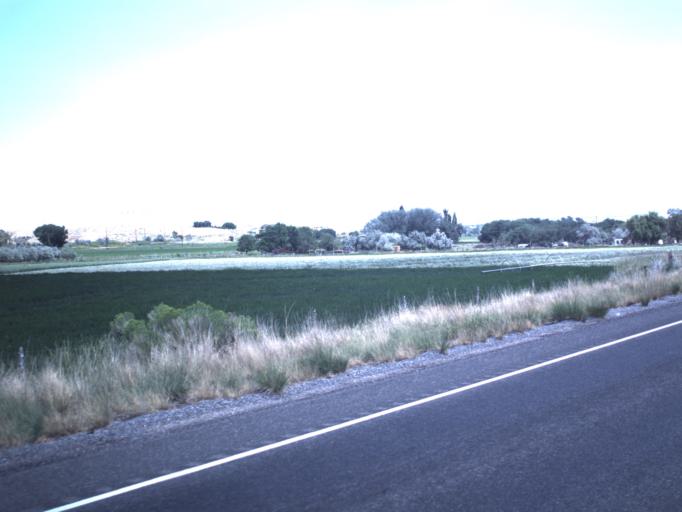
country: US
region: Utah
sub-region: Emery County
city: Huntington
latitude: 39.3486
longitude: -110.9964
